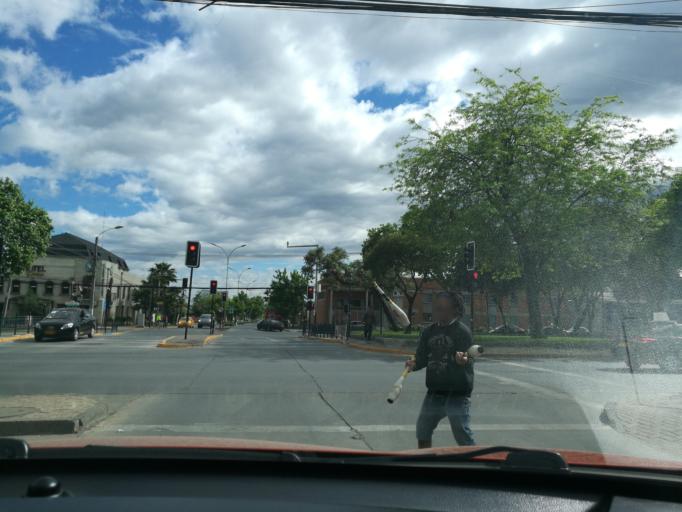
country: CL
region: O'Higgins
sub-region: Provincia de Cachapoal
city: Rancagua
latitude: -34.1667
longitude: -70.7344
